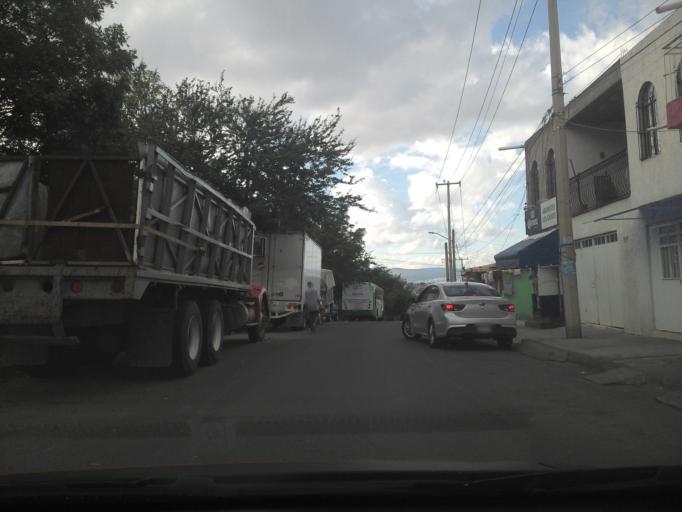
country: MX
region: Jalisco
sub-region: Tlajomulco de Zuniga
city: Altus Bosques
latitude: 20.6165
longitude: -103.3711
